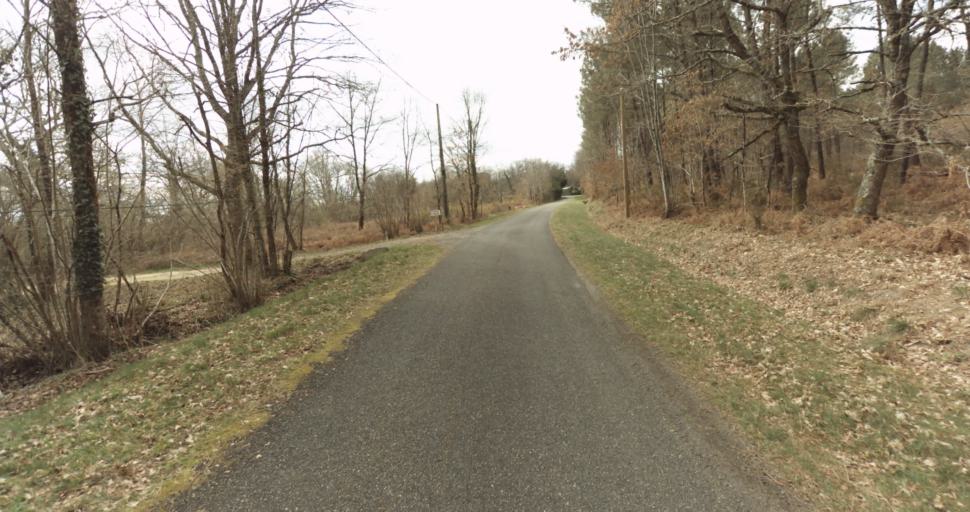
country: FR
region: Aquitaine
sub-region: Departement des Landes
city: Roquefort
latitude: 44.0712
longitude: -0.3943
